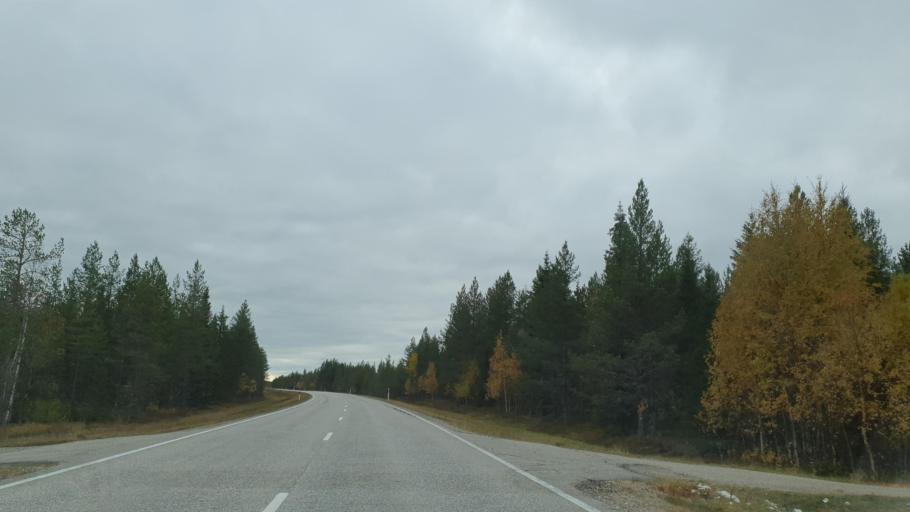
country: FI
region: Northern Ostrobothnia
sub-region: Oulunkaari
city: Pudasjaervi
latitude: 65.5921
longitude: 26.7228
